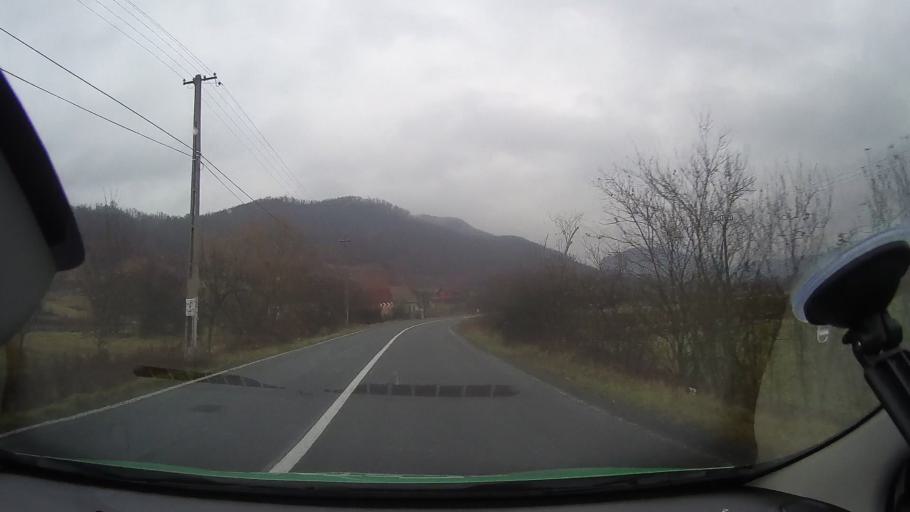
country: RO
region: Arad
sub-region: Comuna Plescuta
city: Plescuta
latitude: 46.2979
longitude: 22.4255
